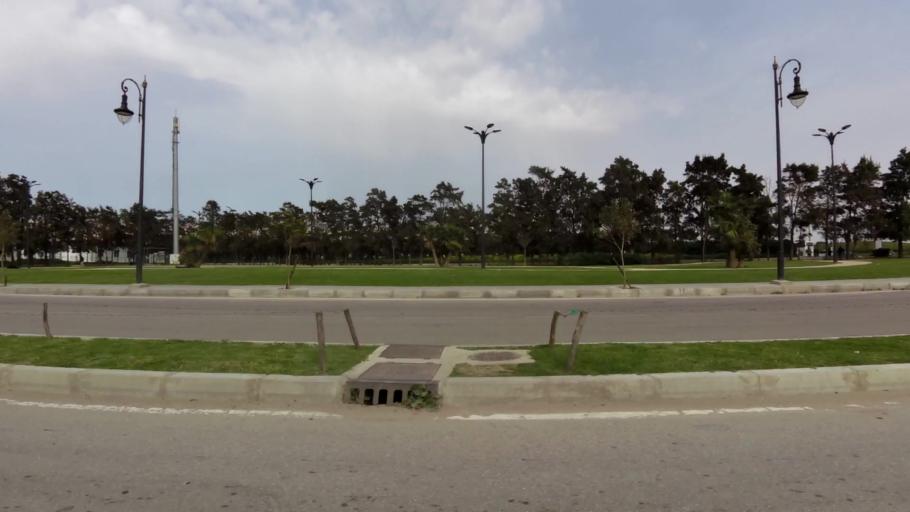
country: MA
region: Tanger-Tetouan
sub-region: Tanger-Assilah
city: Boukhalef
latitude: 35.7291
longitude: -5.8833
